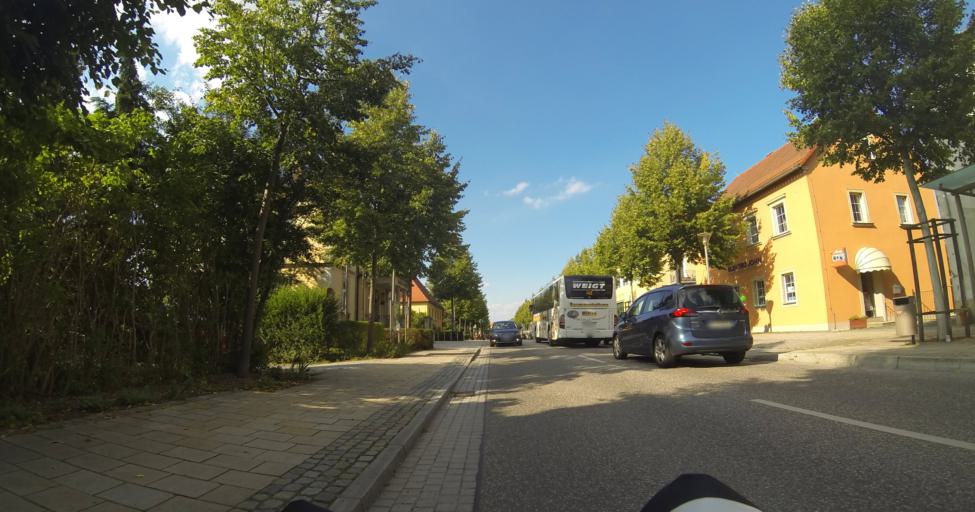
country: DE
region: Saxony
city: Moritzburg
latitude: 51.1602
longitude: 13.6801
